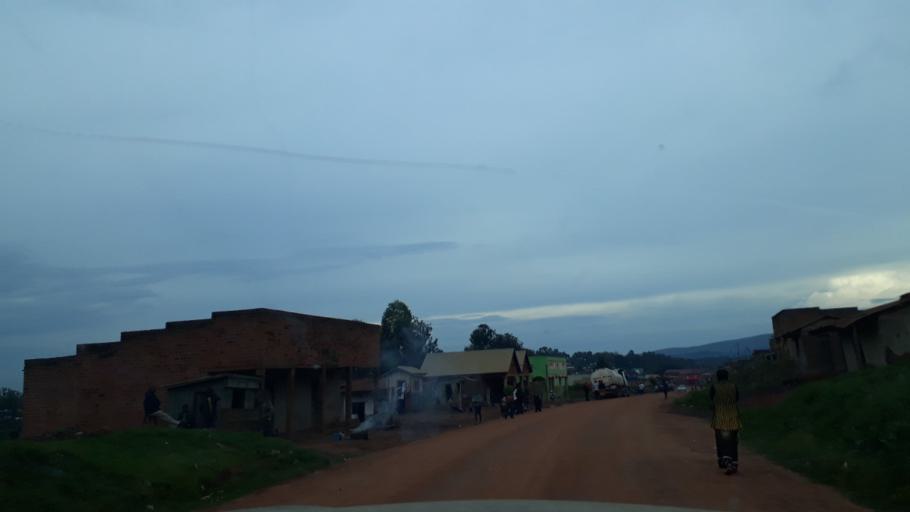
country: UG
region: Northern Region
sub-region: Zombo District
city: Paidha
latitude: 2.2227
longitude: 30.7897
